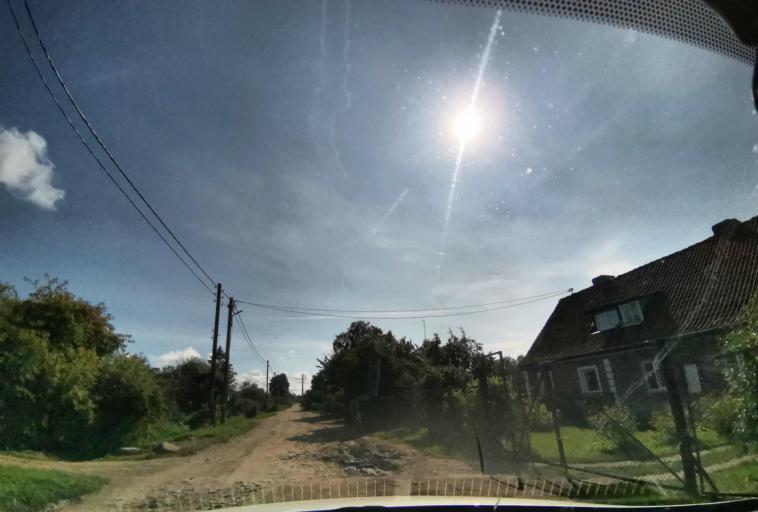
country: RU
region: Kaliningrad
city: Chernyakhovsk
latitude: 54.6582
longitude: 21.8407
